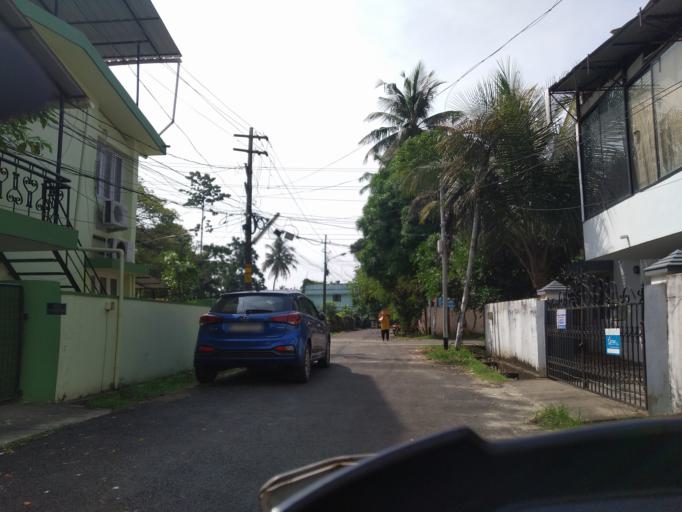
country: IN
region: Kerala
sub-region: Ernakulam
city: Cochin
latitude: 9.9626
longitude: 76.2943
